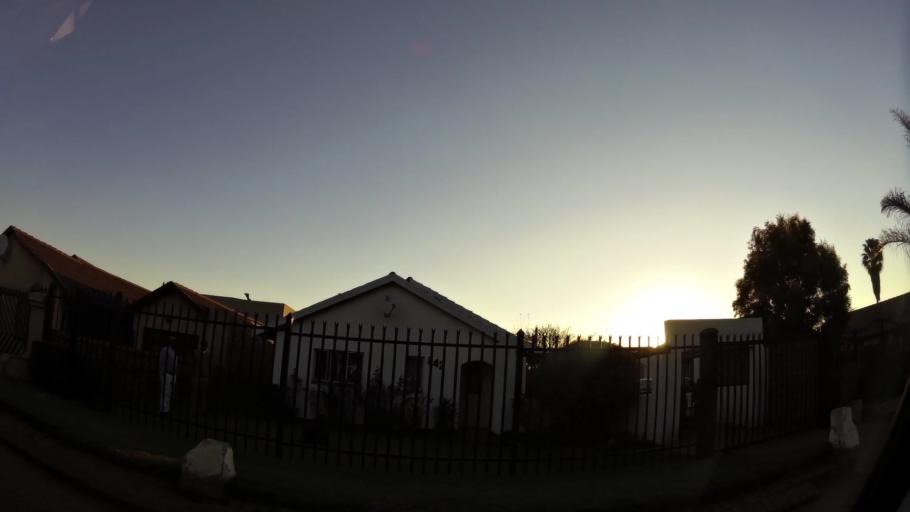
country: ZA
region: Gauteng
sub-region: City of Tshwane Metropolitan Municipality
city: Cullinan
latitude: -25.7130
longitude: 28.3898
